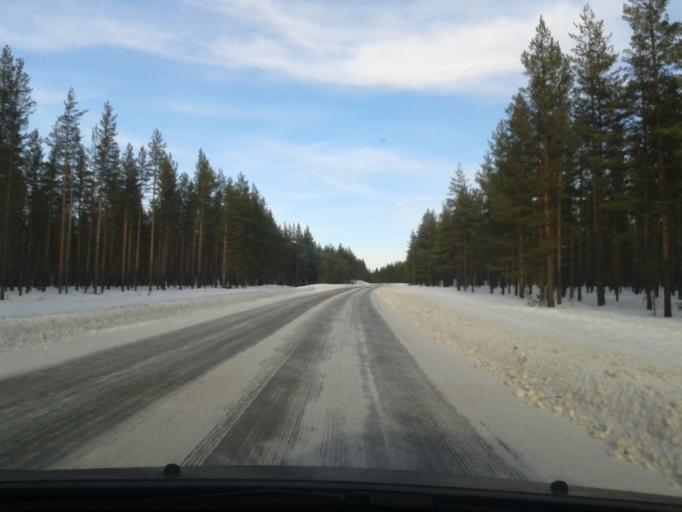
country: SE
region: Vaesternorrland
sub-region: OErnskoeldsviks Kommun
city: Bredbyn
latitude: 63.6117
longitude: 17.9019
